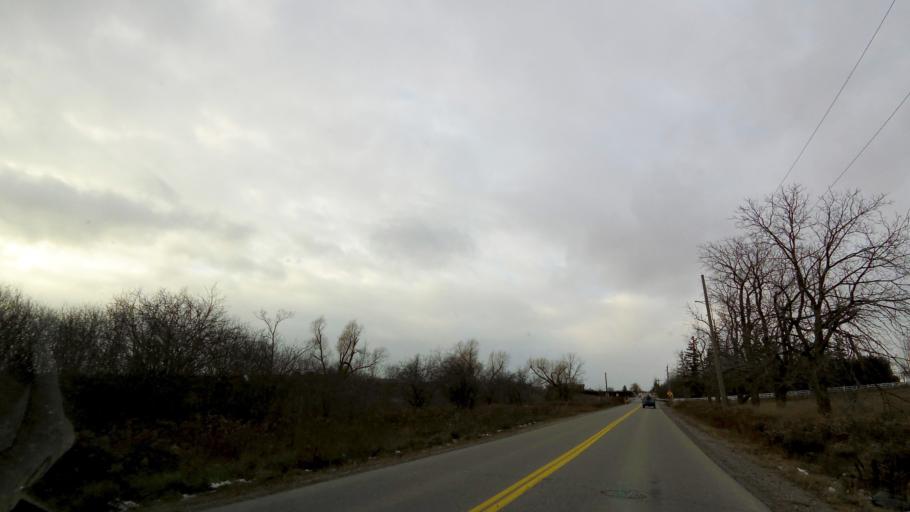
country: CA
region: Ontario
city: Brampton
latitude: 43.8193
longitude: -79.7034
